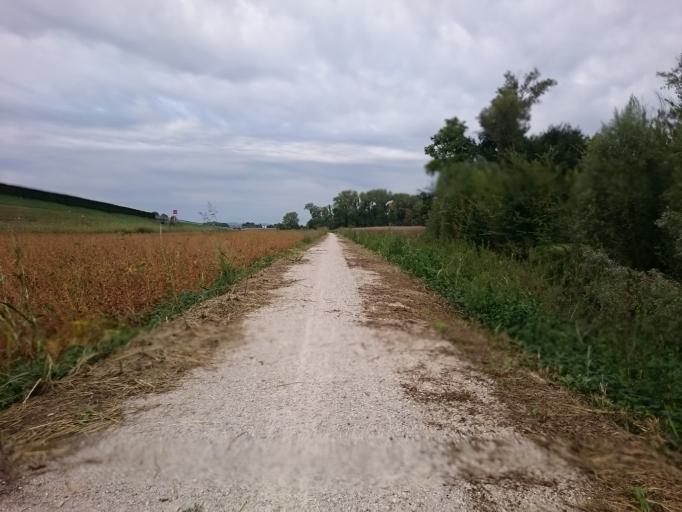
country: IT
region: Veneto
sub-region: Provincia di Vicenza
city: Grisignano di Zocco
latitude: 45.4870
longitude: 11.6833
